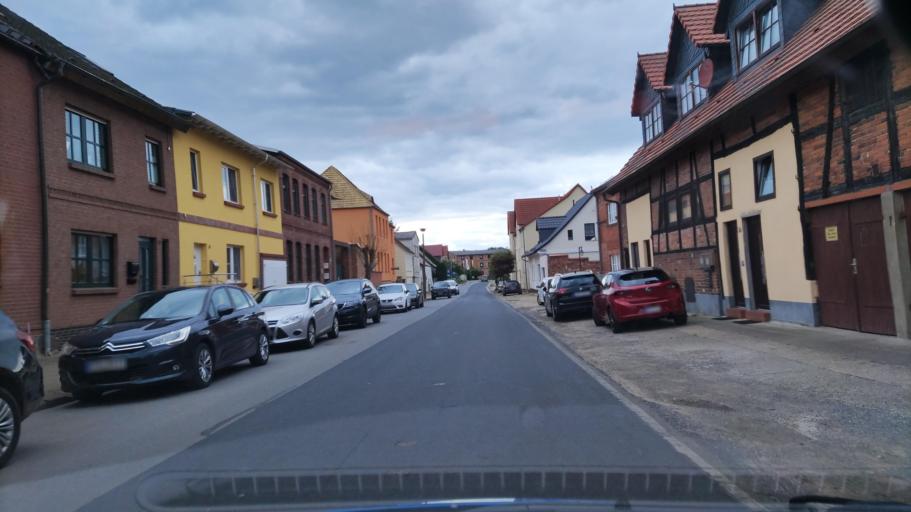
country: DE
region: Mecklenburg-Vorpommern
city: Plau am See
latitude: 53.4560
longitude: 12.2617
